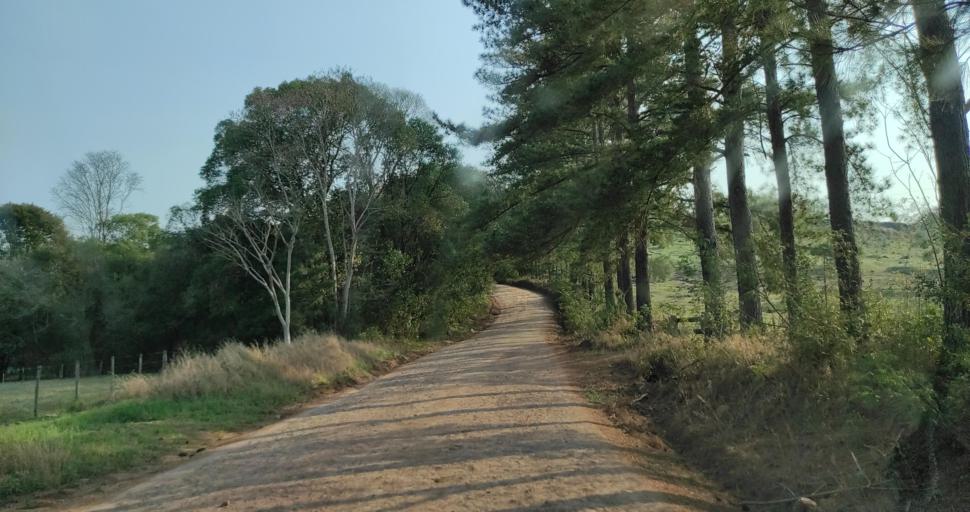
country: AR
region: Misiones
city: Cerro Azul
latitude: -27.6264
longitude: -55.4897
